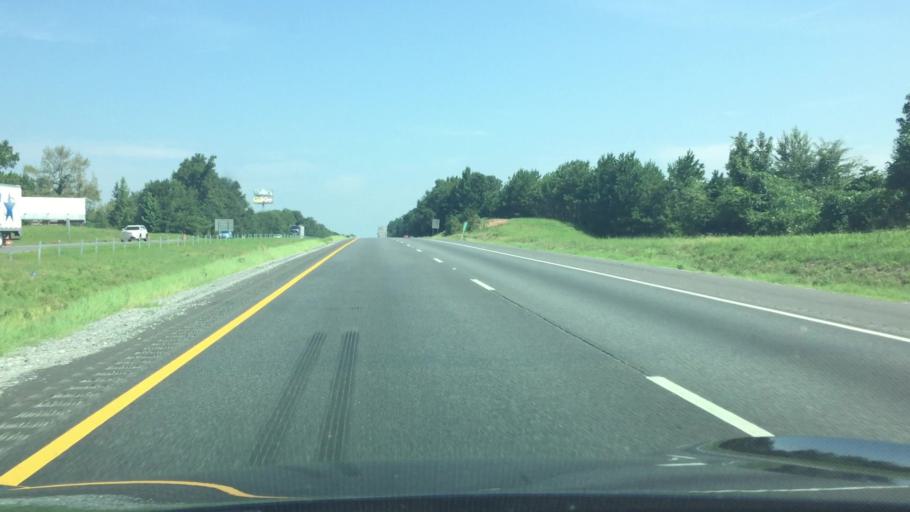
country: US
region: Alabama
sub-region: Chilton County
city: Clanton
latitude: 32.8103
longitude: -86.5832
